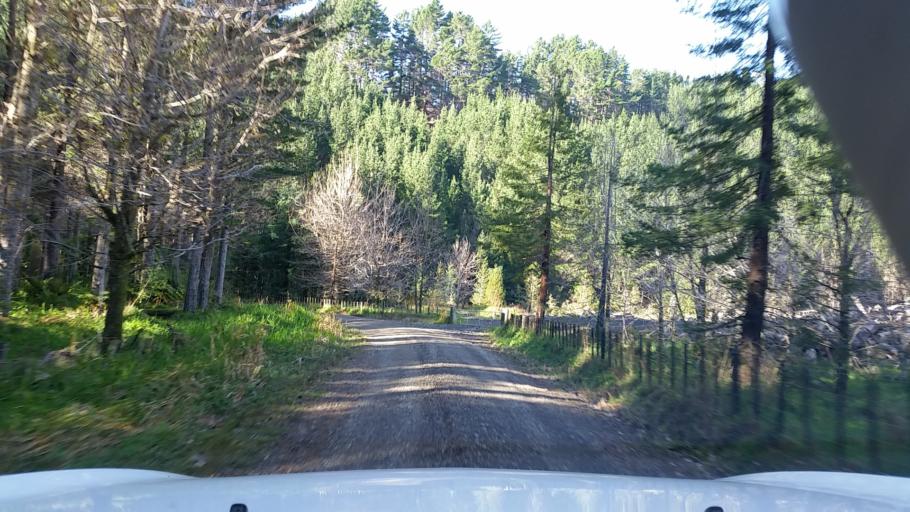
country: NZ
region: Taranaki
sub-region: New Plymouth District
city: Waitara
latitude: -38.9371
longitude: 174.5564
